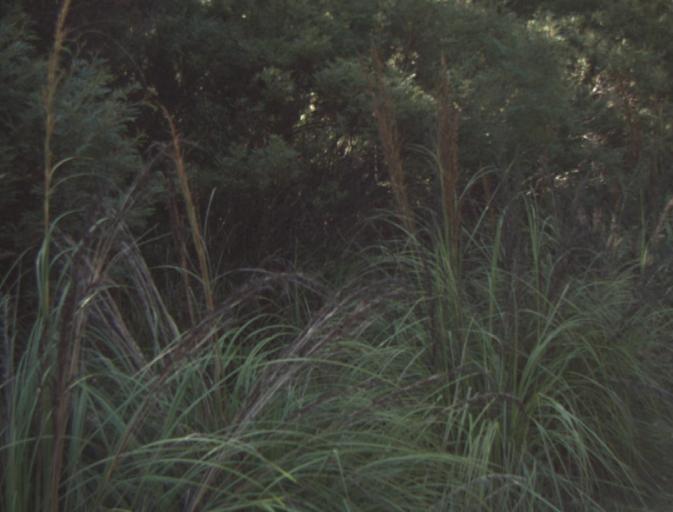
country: AU
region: Tasmania
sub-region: Dorset
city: Bridport
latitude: -41.1522
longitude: 147.2041
